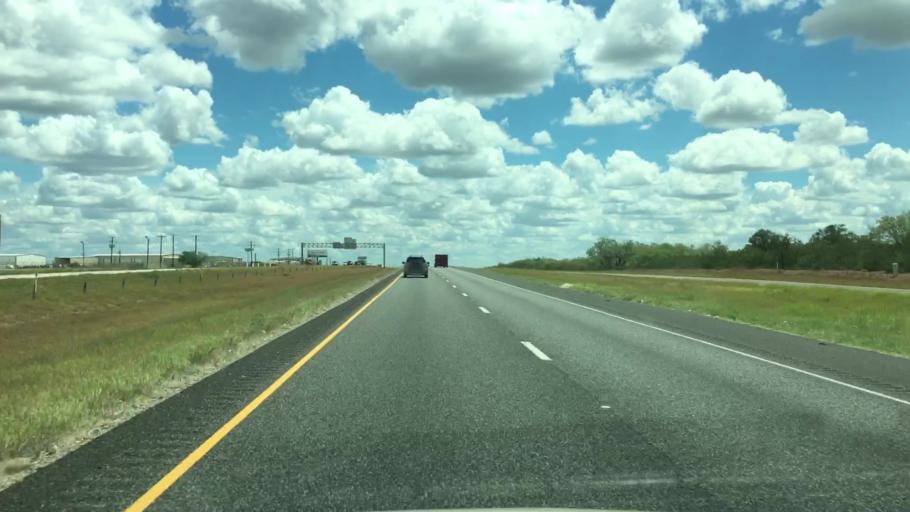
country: US
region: Texas
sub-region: Atascosa County
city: Pleasanton
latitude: 28.8941
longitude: -98.4134
